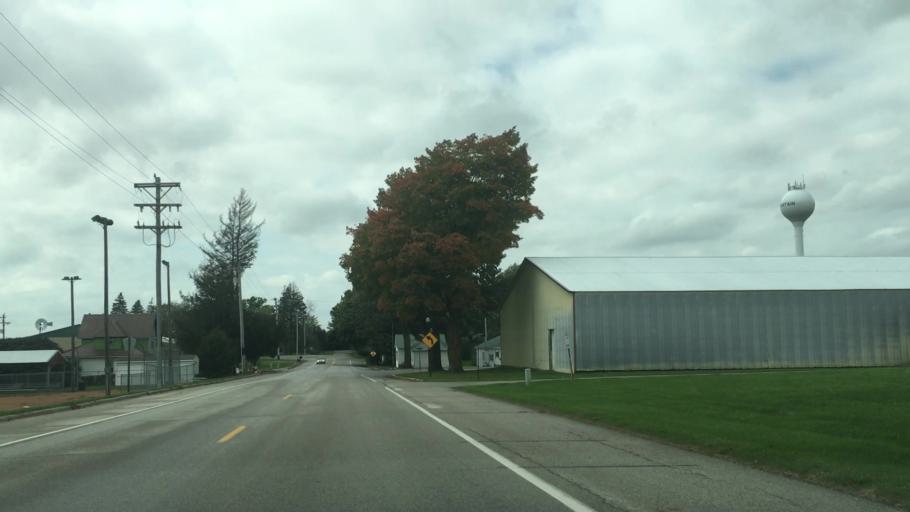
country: US
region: Minnesota
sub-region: Fillmore County
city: Preston
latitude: 43.7389
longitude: -92.1352
